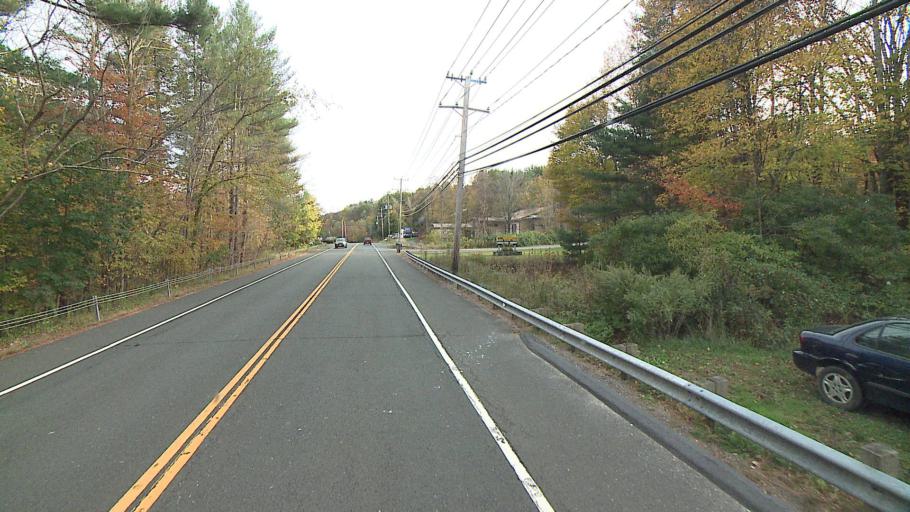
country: US
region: Connecticut
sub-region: Litchfield County
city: New Hartford Center
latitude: 41.9058
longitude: -72.9984
